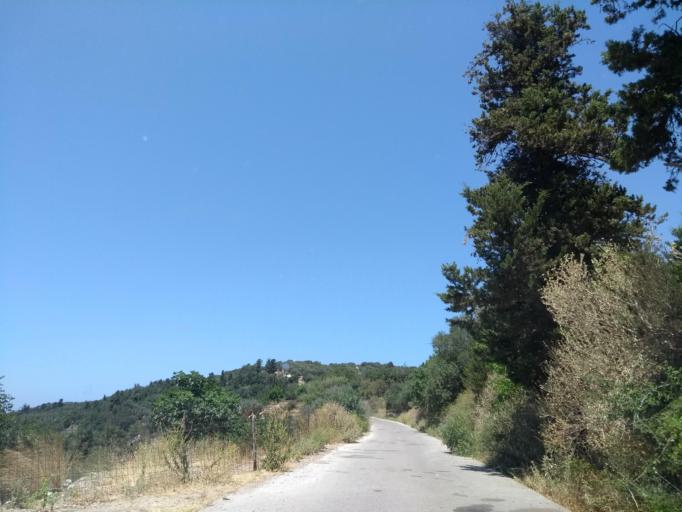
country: GR
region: Crete
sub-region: Nomos Chanias
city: Georgioupolis
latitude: 35.3196
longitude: 24.3090
